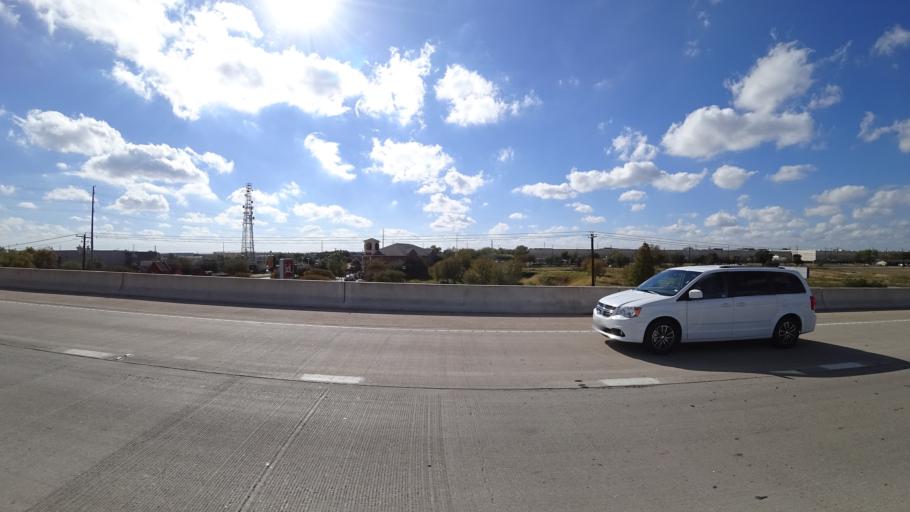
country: US
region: Texas
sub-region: Travis County
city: Austin
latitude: 30.2126
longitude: -97.7153
